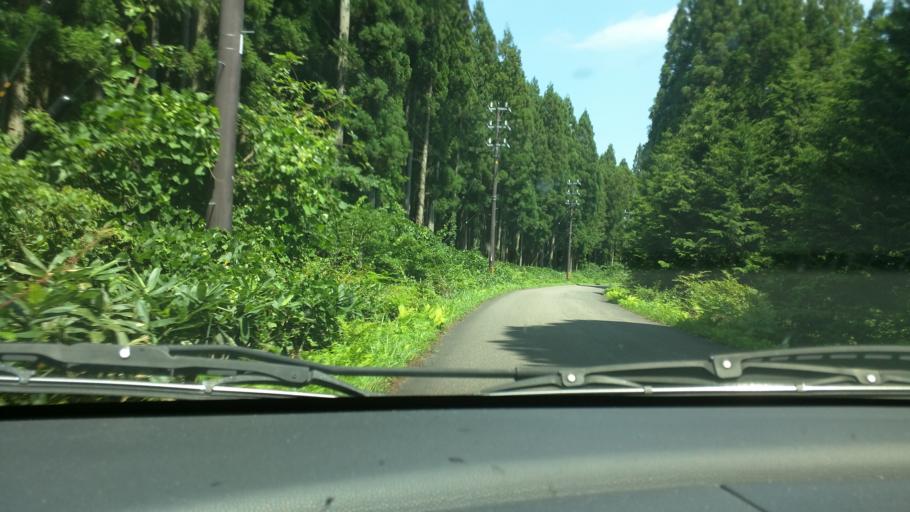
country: JP
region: Fukushima
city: Inawashiro
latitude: 37.3642
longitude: 140.0579
